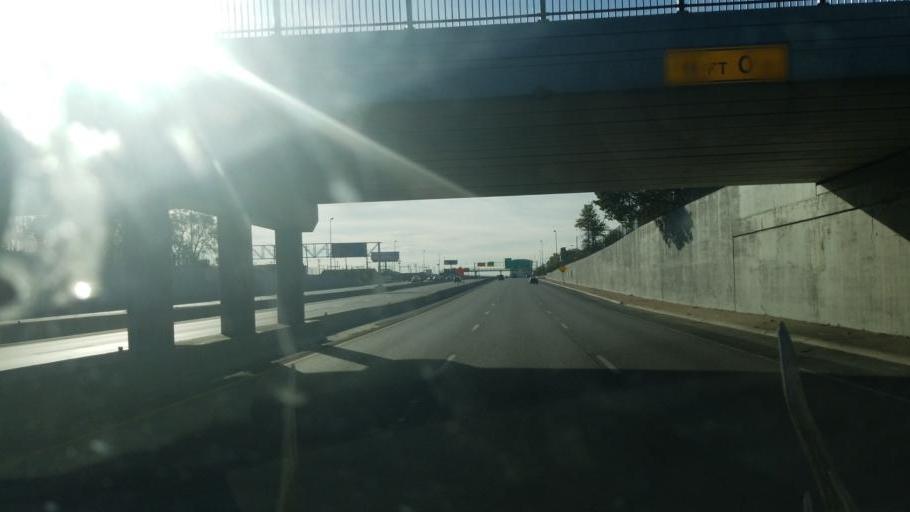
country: US
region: Missouri
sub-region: City of Saint Louis
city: St. Louis
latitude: 38.6532
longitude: -90.1941
